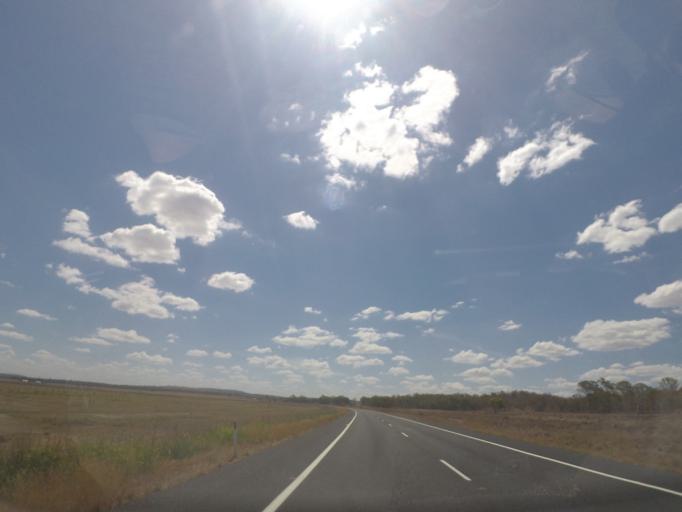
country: AU
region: Queensland
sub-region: Southern Downs
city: Warwick
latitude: -28.1799
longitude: 151.7862
